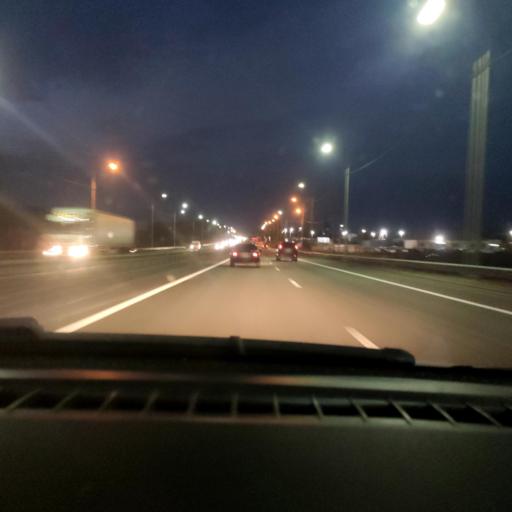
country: RU
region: Voronezj
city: Ramon'
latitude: 51.9408
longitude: 39.2217
